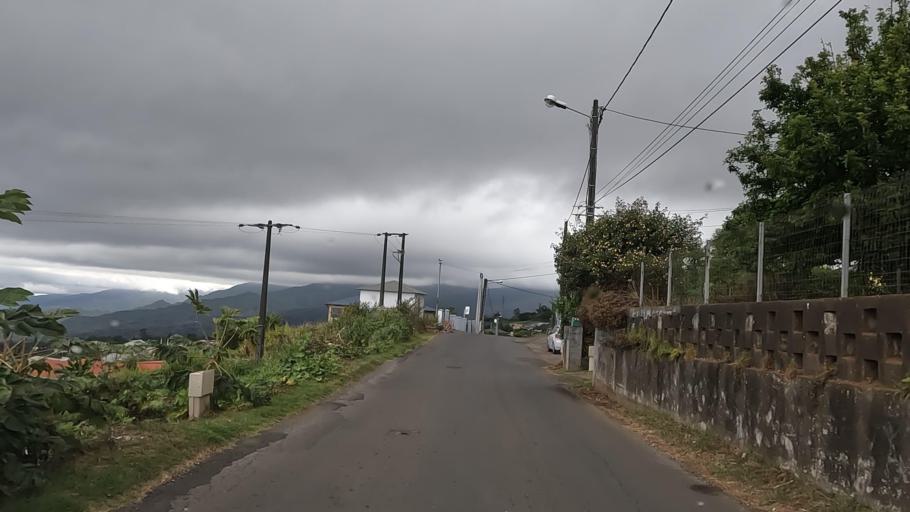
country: RE
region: Reunion
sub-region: Reunion
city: Le Tampon
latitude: -21.2216
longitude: 55.5365
